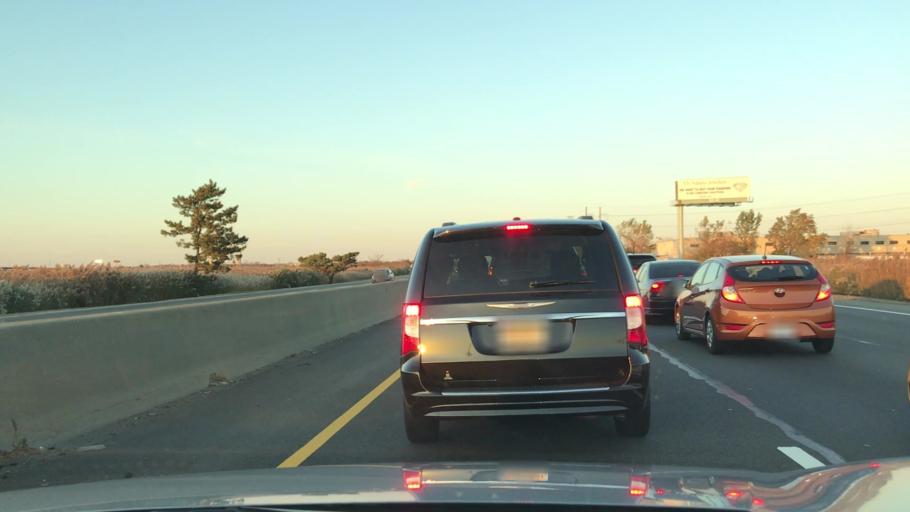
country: US
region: New Jersey
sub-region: Hudson County
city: North Bergen
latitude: 40.8061
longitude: -74.0323
